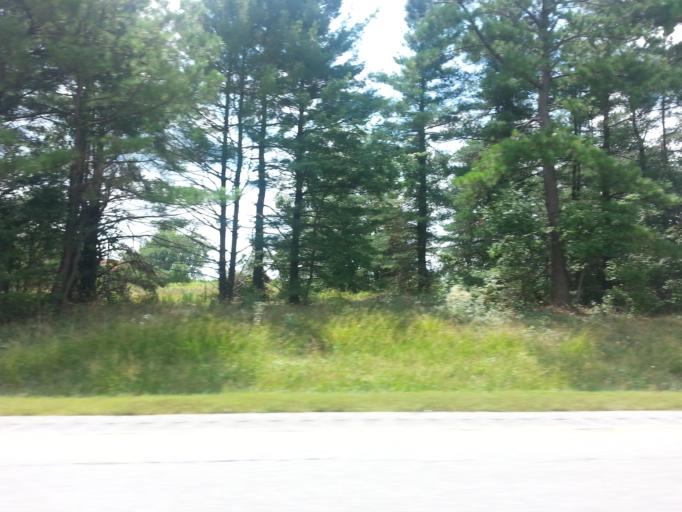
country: US
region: Tennessee
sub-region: Putnam County
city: Monterey
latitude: 36.0526
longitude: -85.1658
